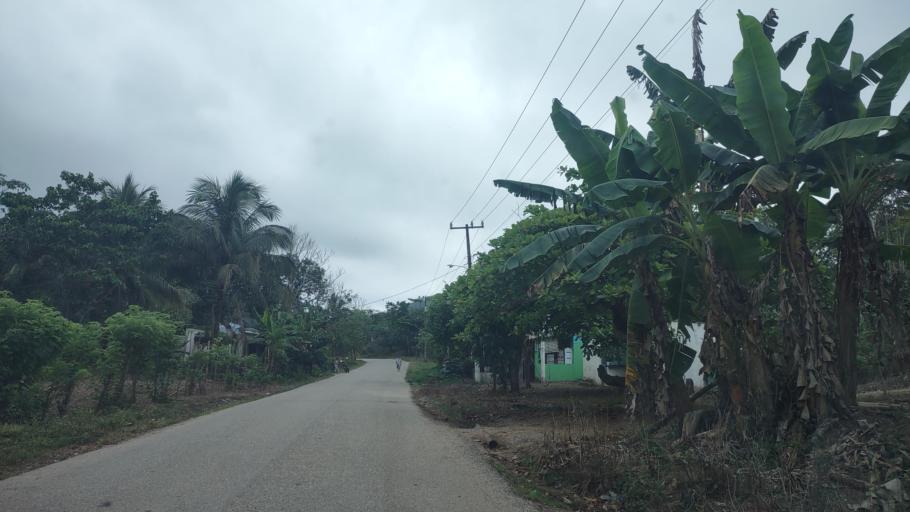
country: MX
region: Veracruz
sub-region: Uxpanapa
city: Poblado 10
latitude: 17.4782
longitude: -94.1195
